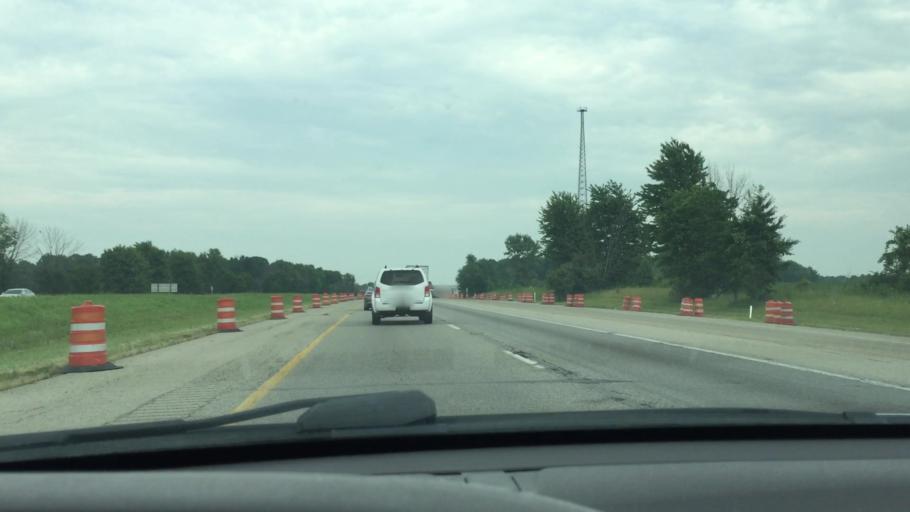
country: US
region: Ohio
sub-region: Warren County
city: Morrow
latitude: 39.4315
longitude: -84.0765
